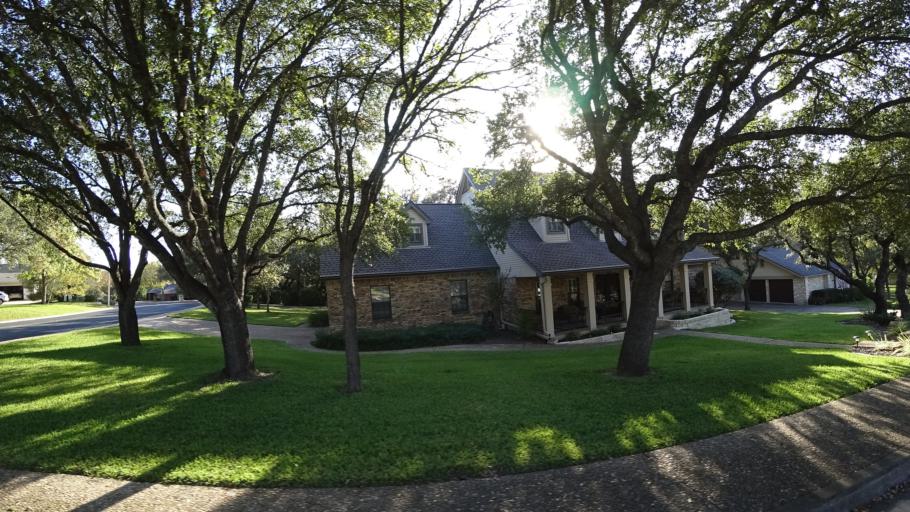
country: US
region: Texas
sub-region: Williamson County
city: Anderson Mill
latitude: 30.4328
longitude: -97.8112
